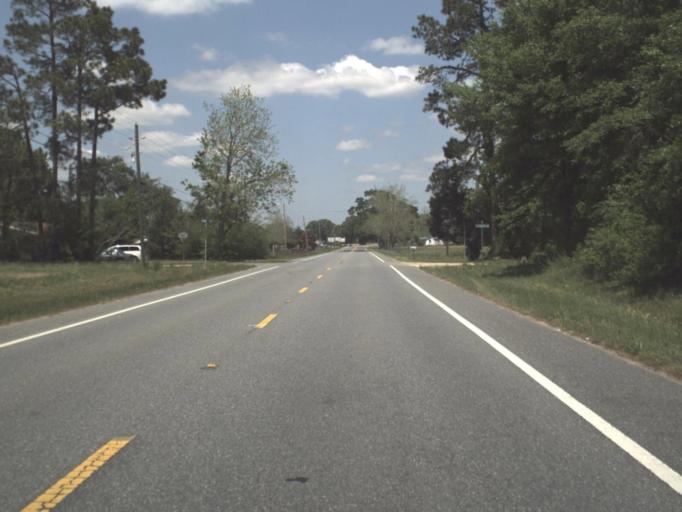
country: US
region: Florida
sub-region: Santa Rosa County
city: Point Baker
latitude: 30.8775
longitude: -87.0523
